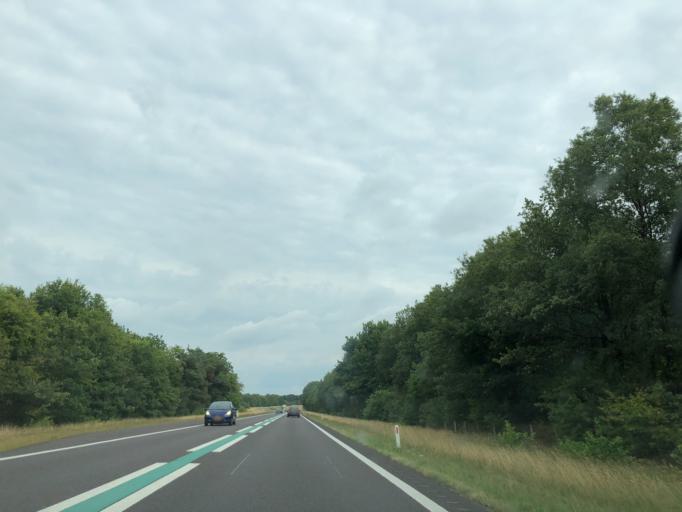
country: NL
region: Drenthe
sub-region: Gemeente Tynaarlo
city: Zuidlaren
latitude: 53.0729
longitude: 6.6855
